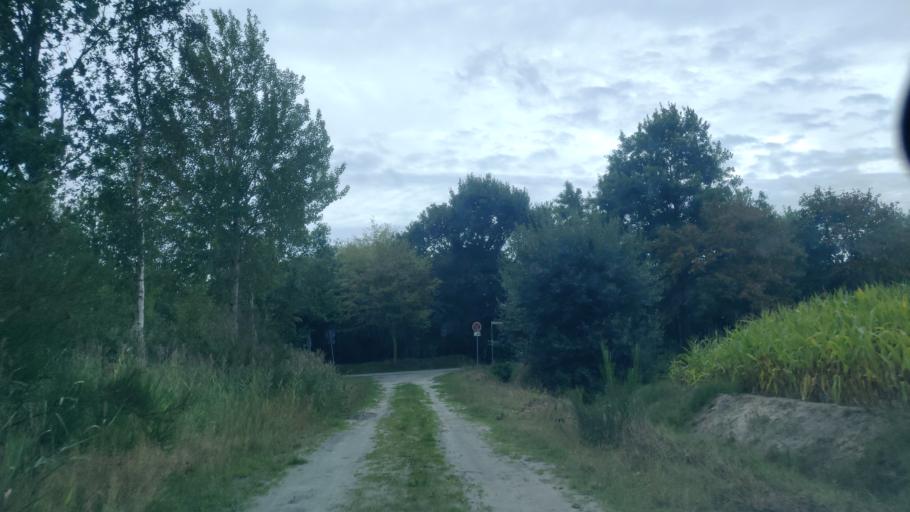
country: DE
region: Lower Saxony
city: Aurich
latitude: 53.5275
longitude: 7.4784
